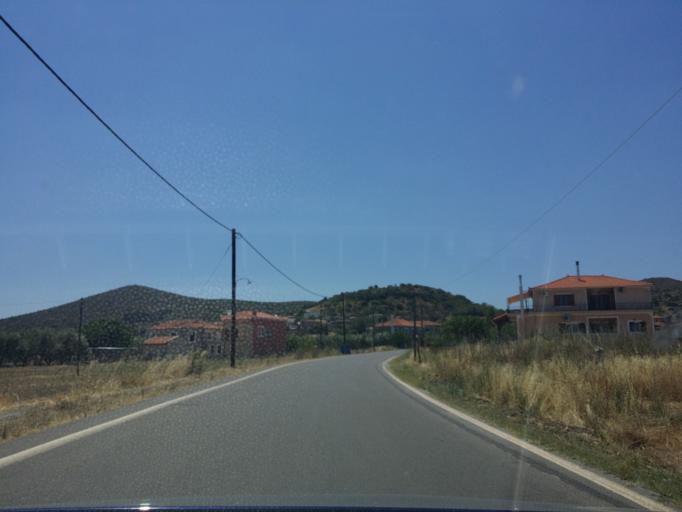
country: GR
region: Peloponnese
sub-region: Nomos Lakonias
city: Kato Glikovrisi
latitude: 36.8860
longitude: 22.8001
